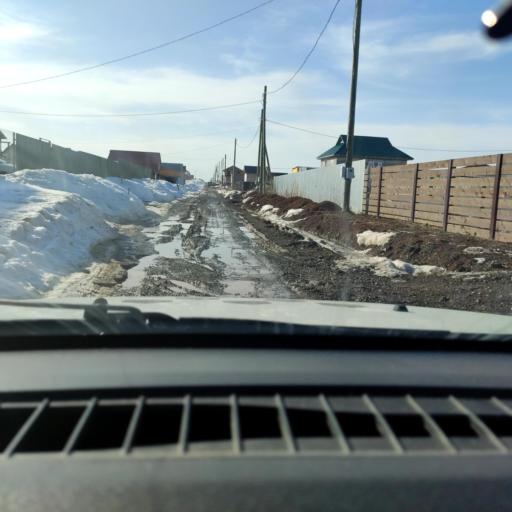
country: RU
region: Perm
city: Kultayevo
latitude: 57.8714
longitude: 55.9758
